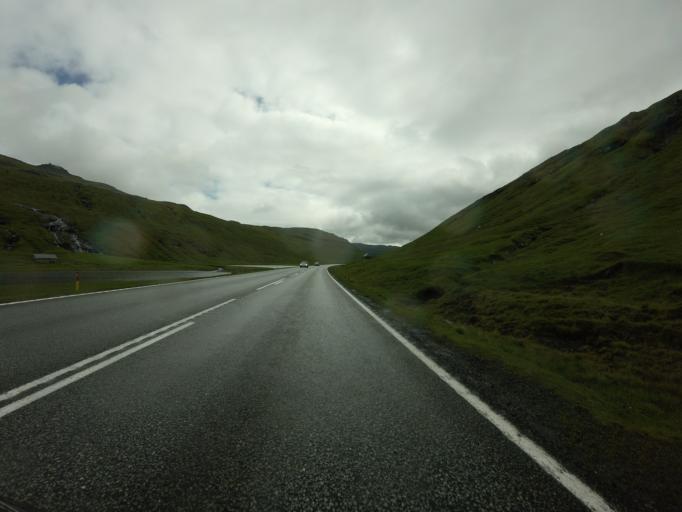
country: FO
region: Streymoy
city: Kollafjordhur
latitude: 62.1267
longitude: -7.0021
